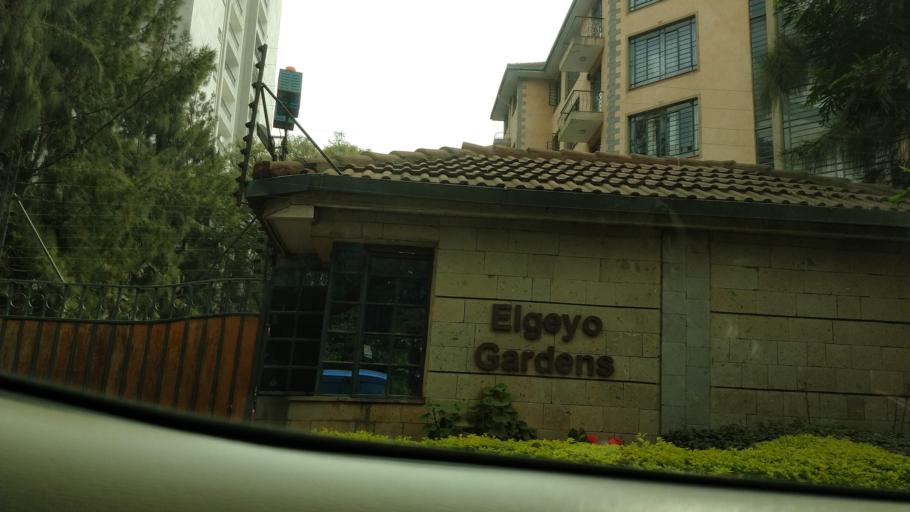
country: KE
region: Nairobi Area
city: Nairobi
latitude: -1.2982
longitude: 36.7794
